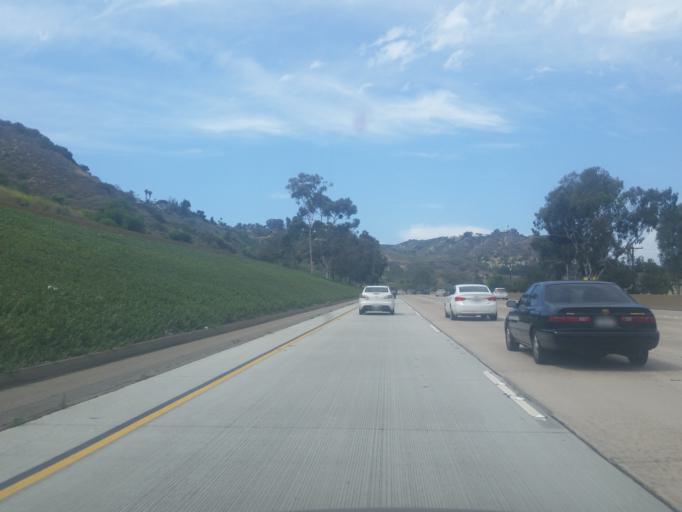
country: US
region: California
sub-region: San Diego County
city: La Jolla
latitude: 32.8206
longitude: -117.2274
